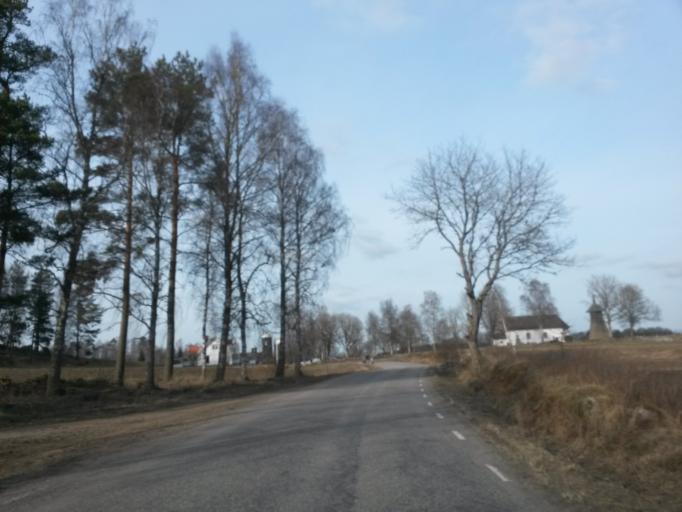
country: SE
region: Vaestra Goetaland
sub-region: Vargarda Kommun
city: Jonstorp
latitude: 57.9920
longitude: 12.7692
